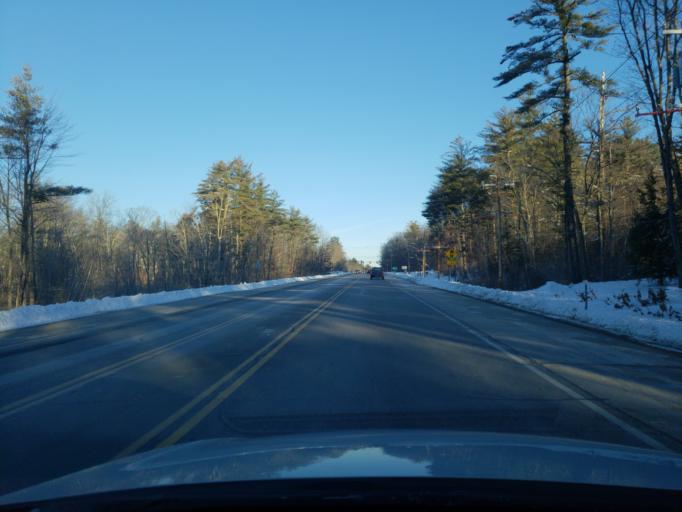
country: US
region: New Hampshire
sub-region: Hillsborough County
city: Pinardville
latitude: 42.9880
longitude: -71.5228
